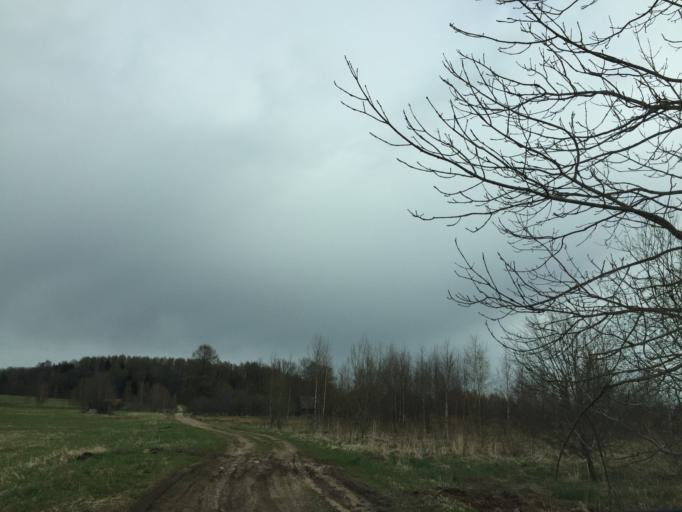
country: LV
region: Priekuli
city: Priekuli
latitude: 57.2938
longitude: 25.3335
